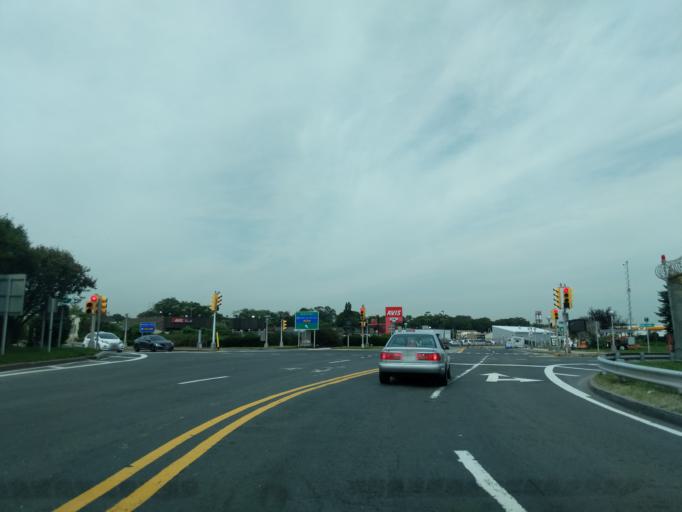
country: US
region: New York
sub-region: Queens County
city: Long Island City
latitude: 40.7684
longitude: -73.8857
